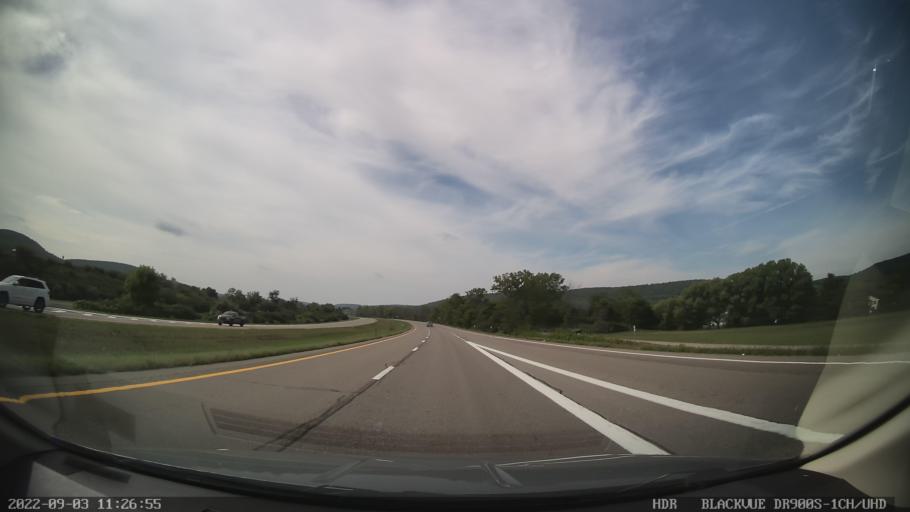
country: US
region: New York
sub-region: Steuben County
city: Gang Mills
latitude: 42.1400
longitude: -77.1195
